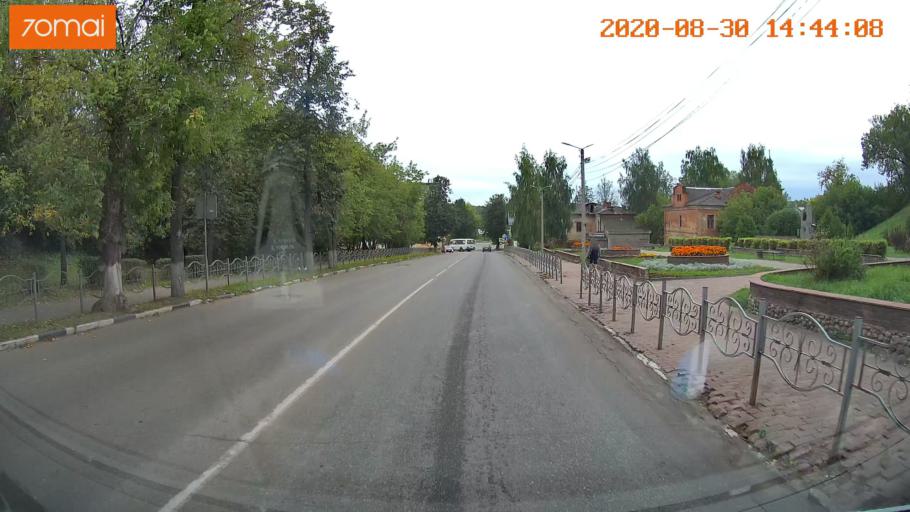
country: RU
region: Ivanovo
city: Kineshma
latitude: 57.4436
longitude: 42.1634
